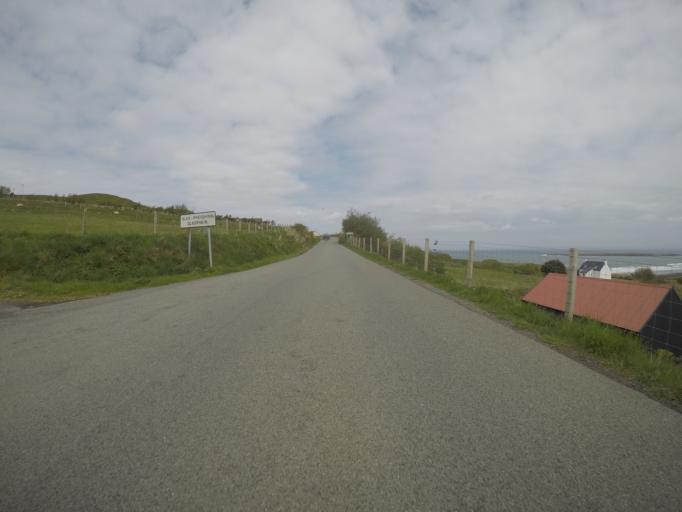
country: GB
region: Scotland
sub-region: Highland
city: Portree
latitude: 57.6345
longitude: -6.2408
